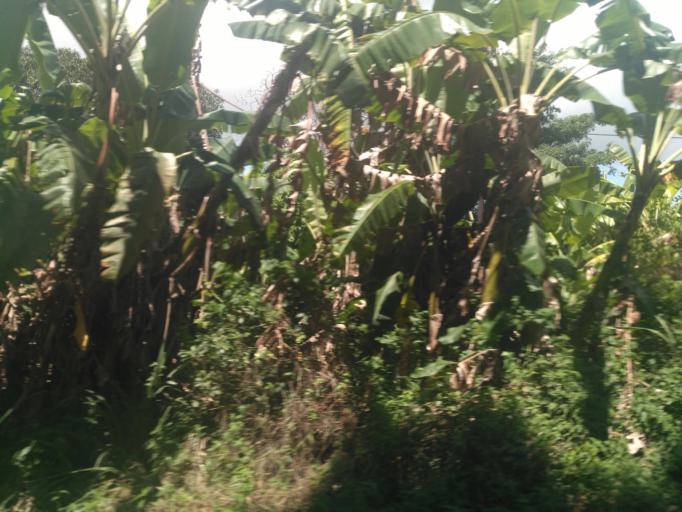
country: TZ
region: Zanzibar North
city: Gamba
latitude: -5.9389
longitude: 39.3400
